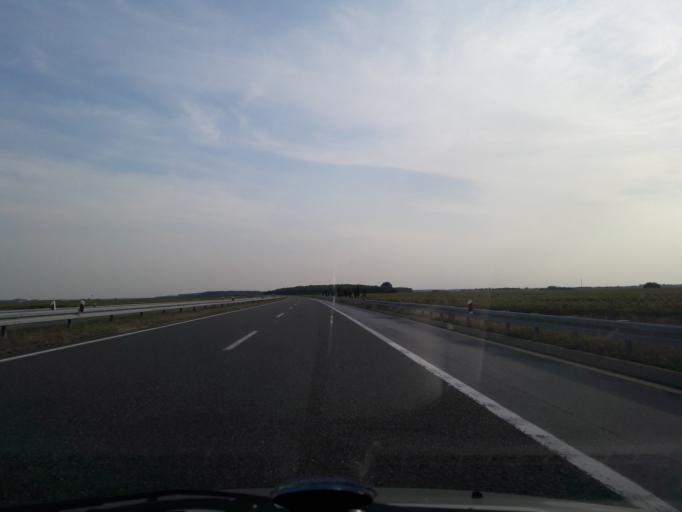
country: HR
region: Osjecko-Baranjska
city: Cepin
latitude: 45.5310
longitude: 18.5168
